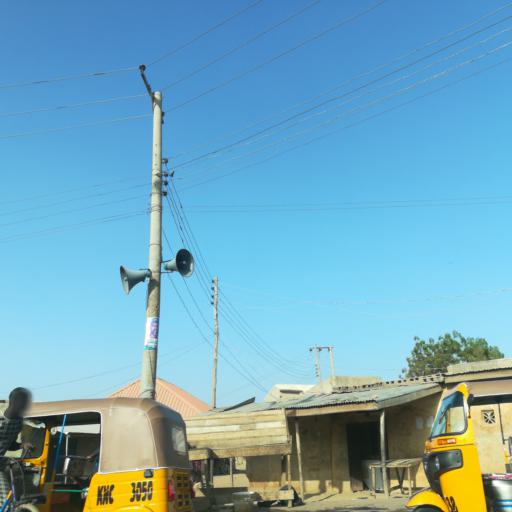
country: NG
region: Kano
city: Kano
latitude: 12.0177
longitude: 8.4924
